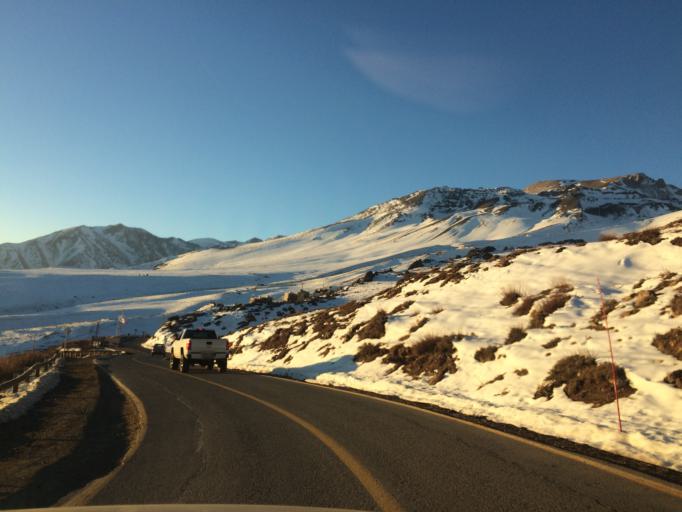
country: CL
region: Santiago Metropolitan
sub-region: Provincia de Santiago
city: Villa Presidente Frei, Nunoa, Santiago, Chile
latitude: -33.3451
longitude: -70.2945
